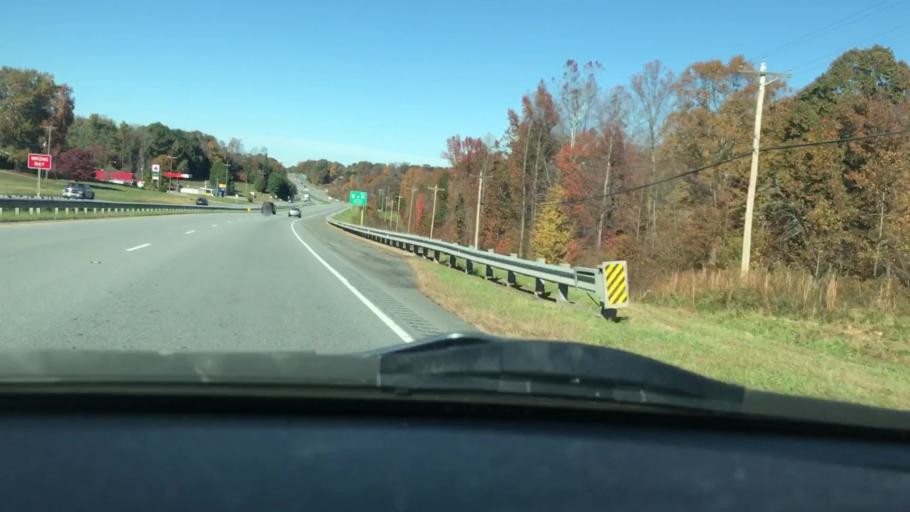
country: US
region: North Carolina
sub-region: Rockingham County
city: Madison
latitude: 36.3569
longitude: -79.9465
